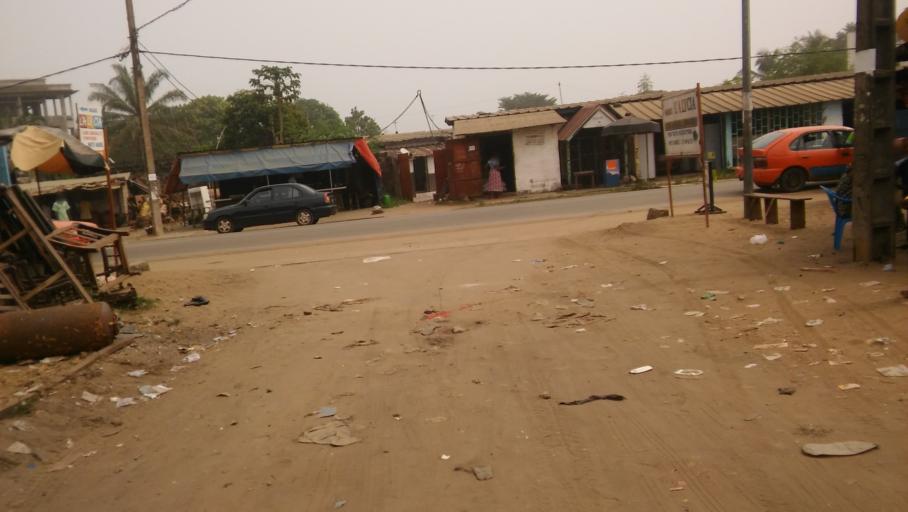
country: CI
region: Sud-Comoe
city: Grand-Bassam
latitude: 5.2127
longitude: -3.7325
